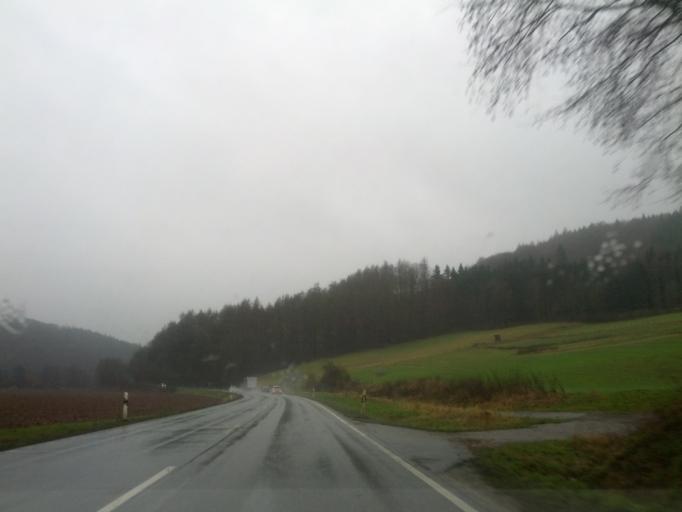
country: DE
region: Hesse
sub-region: Regierungsbezirk Kassel
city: Sontra
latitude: 51.0995
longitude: 9.9687
